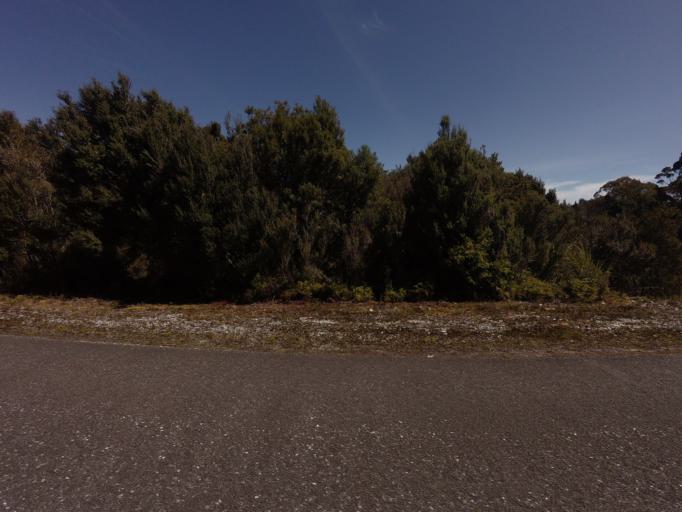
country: AU
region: Tasmania
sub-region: Huon Valley
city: Geeveston
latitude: -42.8334
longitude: 146.1526
